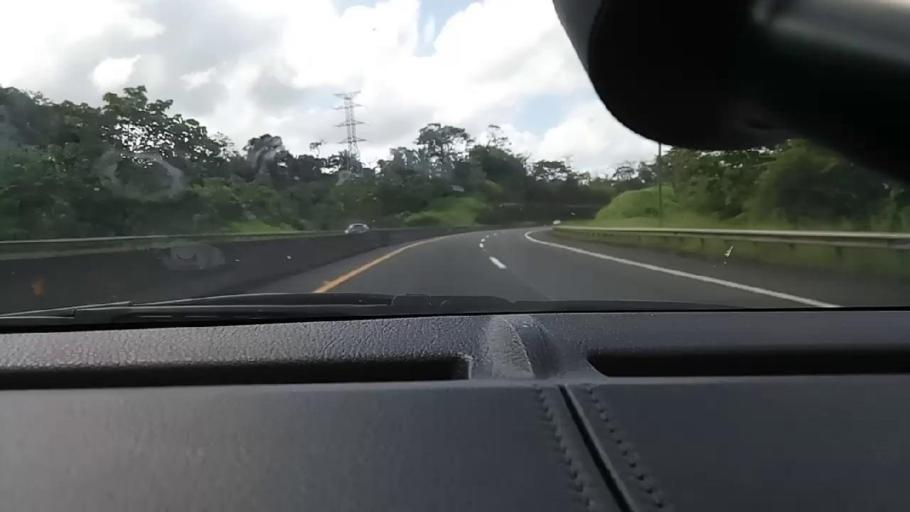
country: PA
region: Colon
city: Las Margaritas
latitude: 9.3312
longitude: -79.8638
